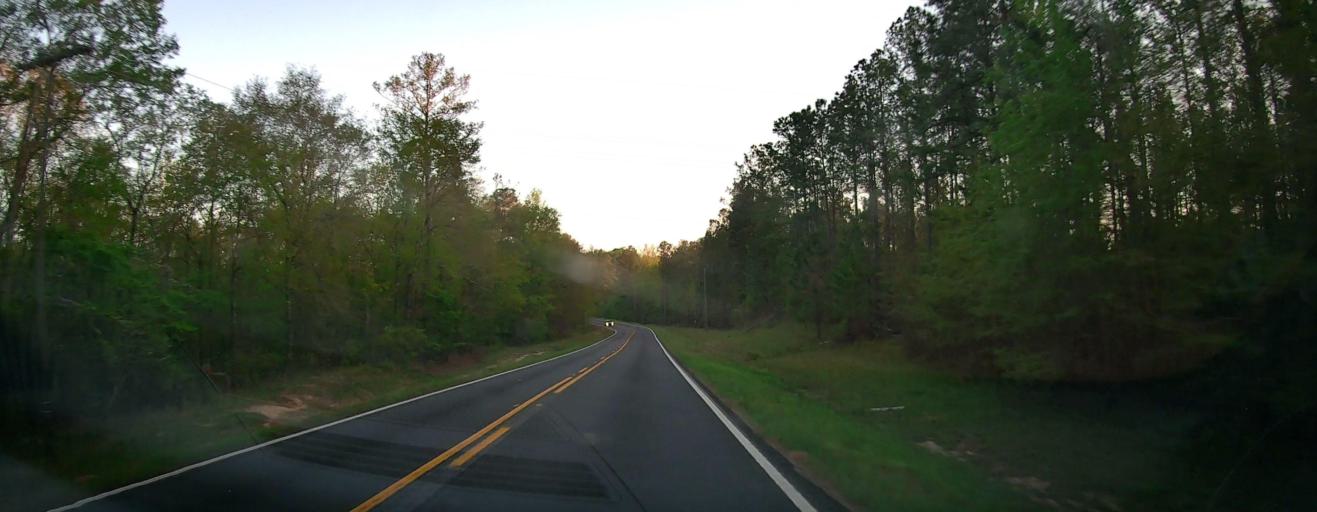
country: US
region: Georgia
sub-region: Marion County
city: Buena Vista
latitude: 32.4349
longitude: -84.5996
